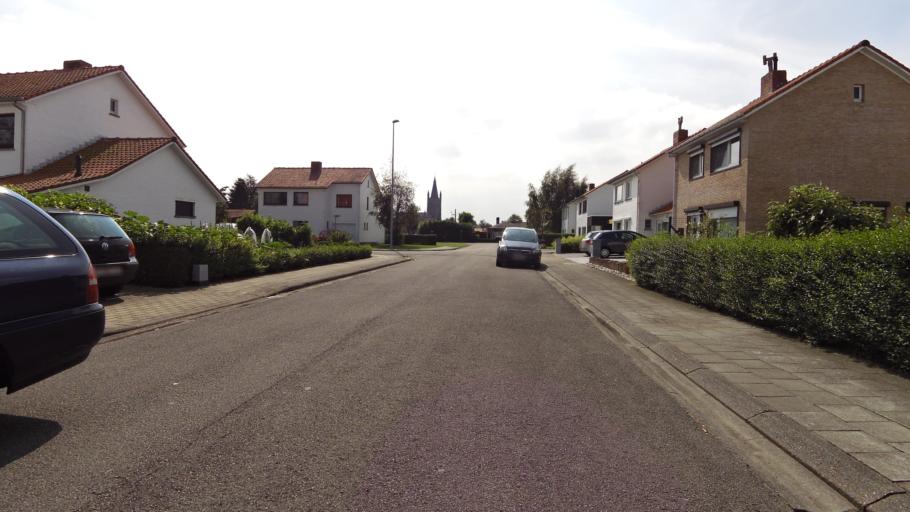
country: BE
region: Flanders
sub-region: Provincie West-Vlaanderen
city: Ostend
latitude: 51.1781
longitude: 2.8806
